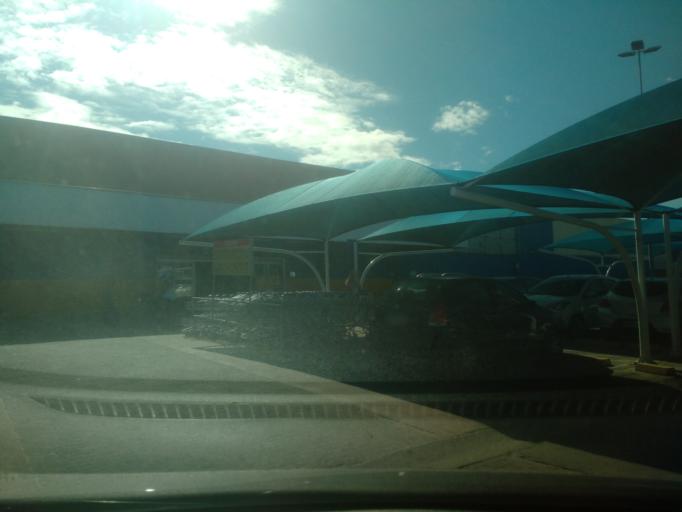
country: BR
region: Alagoas
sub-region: Satuba
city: Satuba
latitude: -9.5726
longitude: -35.7410
